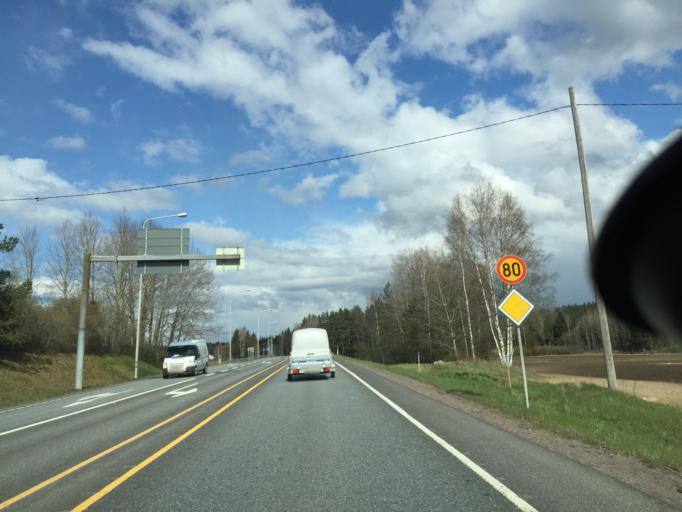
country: FI
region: Uusimaa
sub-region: Raaseporin
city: Karis
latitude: 60.0677
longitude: 23.6930
